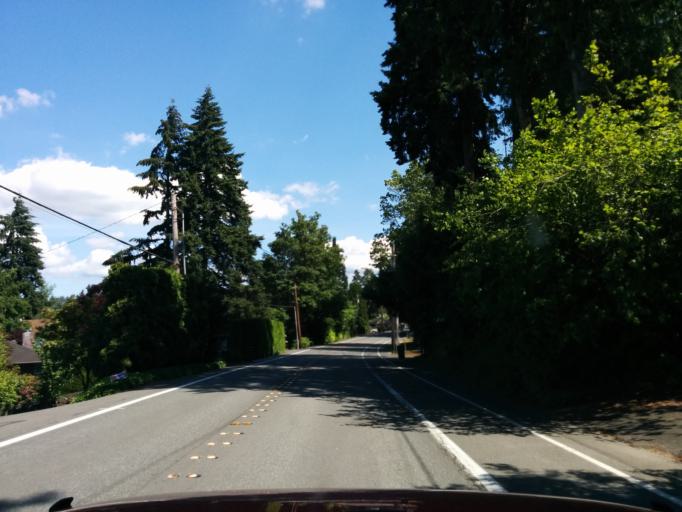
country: US
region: Washington
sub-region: King County
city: Sammamish
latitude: 47.6374
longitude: -122.0952
